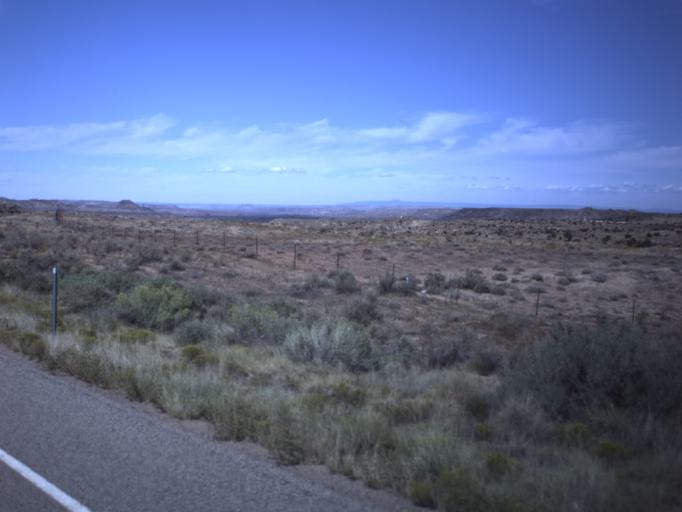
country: US
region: Colorado
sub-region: Montezuma County
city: Towaoc
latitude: 37.1779
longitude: -109.1200
